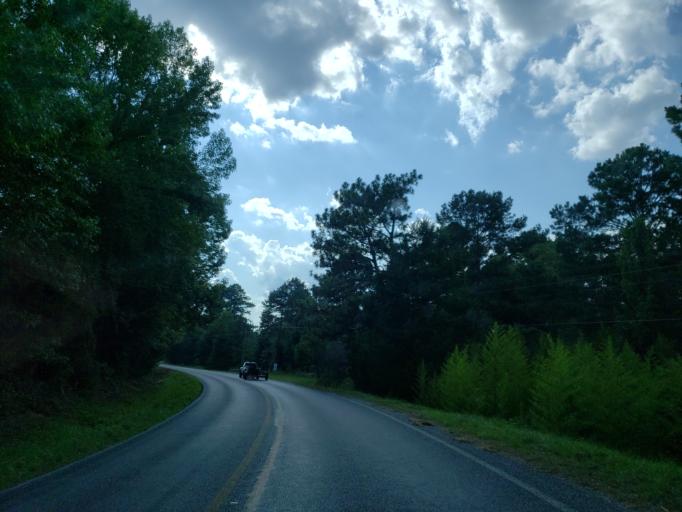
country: US
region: Mississippi
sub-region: Jones County
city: Sharon
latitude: 31.9197
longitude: -89.0208
